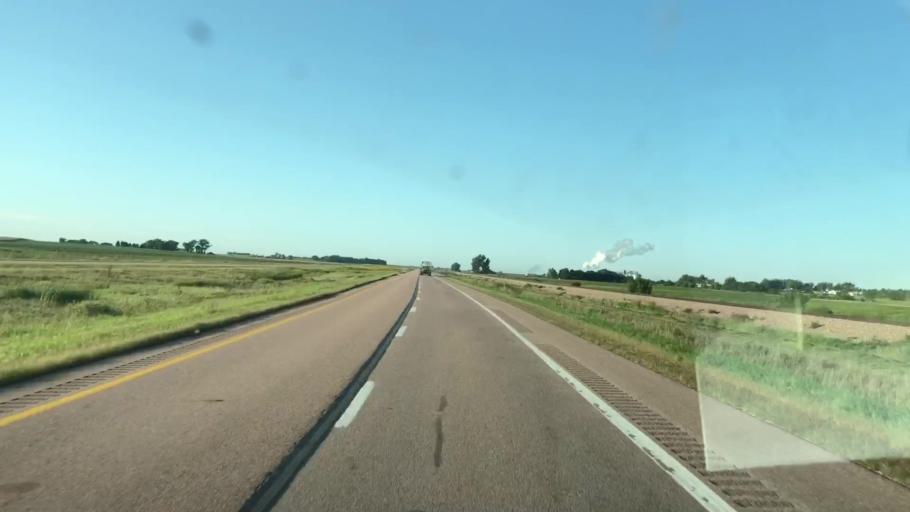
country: US
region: Iowa
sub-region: Osceola County
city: Sibley
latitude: 43.2972
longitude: -95.7943
